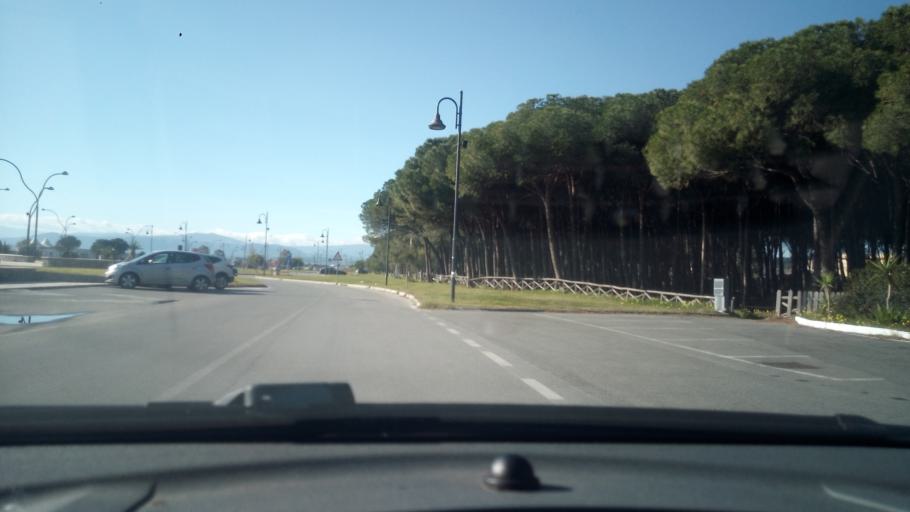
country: IT
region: Calabria
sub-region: Provincia di Catanzaro
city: Barone
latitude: 38.8295
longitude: 16.6400
